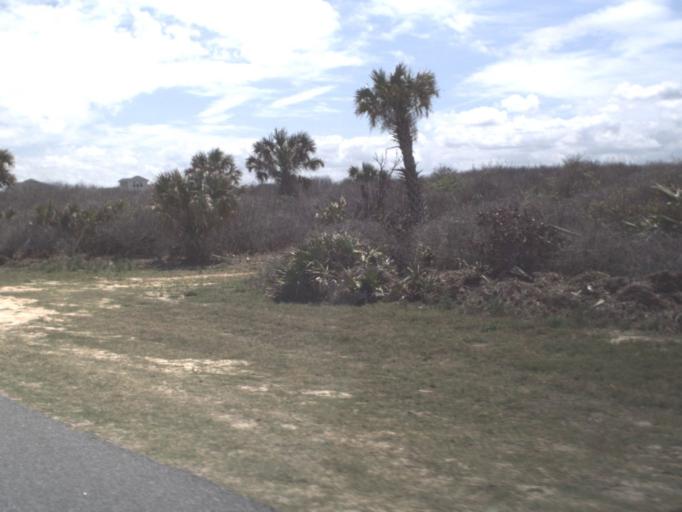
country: US
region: Florida
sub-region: Flagler County
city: Palm Coast
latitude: 29.6588
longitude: -81.2091
